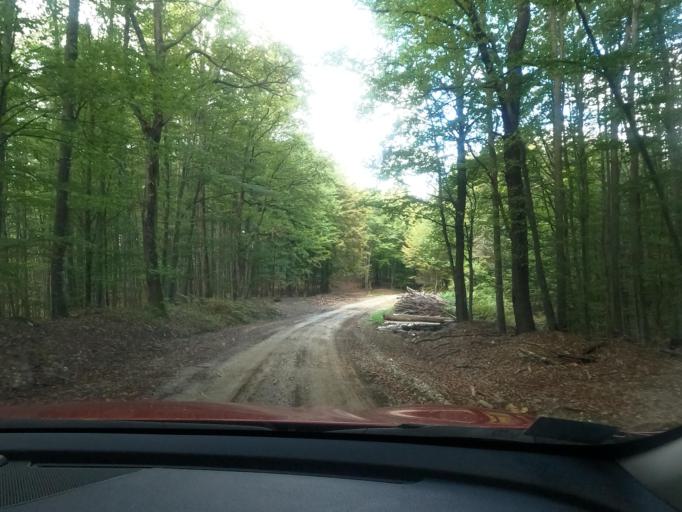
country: BA
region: Federation of Bosnia and Herzegovina
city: Velika Kladusa
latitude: 45.2673
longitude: 15.7784
